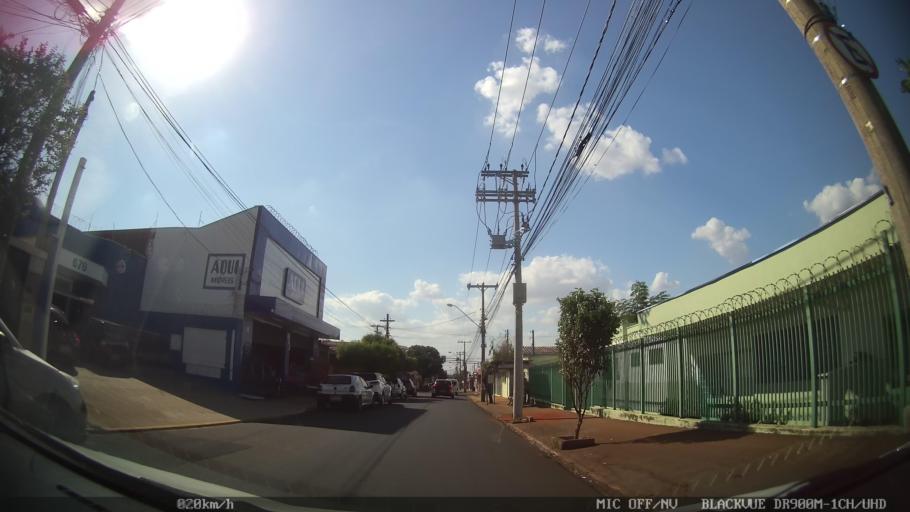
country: BR
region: Sao Paulo
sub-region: Ribeirao Preto
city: Ribeirao Preto
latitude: -21.1879
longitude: -47.8255
